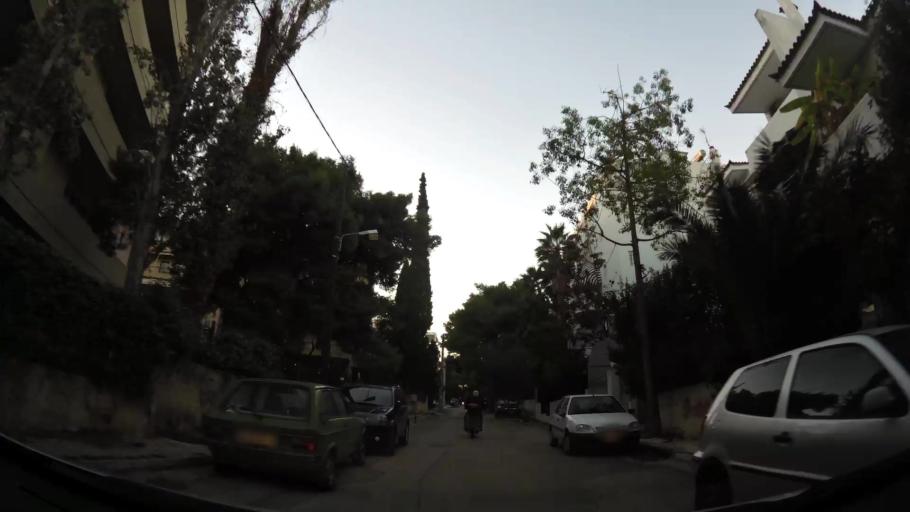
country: GR
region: Attica
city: Pefki
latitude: 38.0599
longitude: 23.7912
